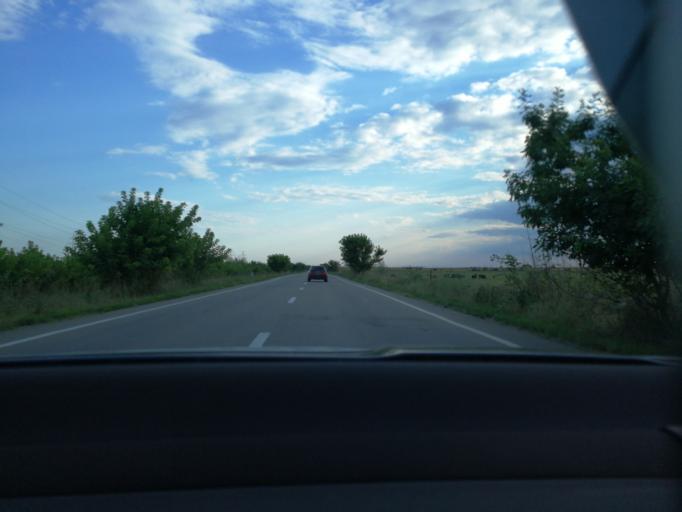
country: RO
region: Prahova
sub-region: Comuna Targsoru Vechi
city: Strejnicu
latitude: 44.8923
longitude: 25.9616
